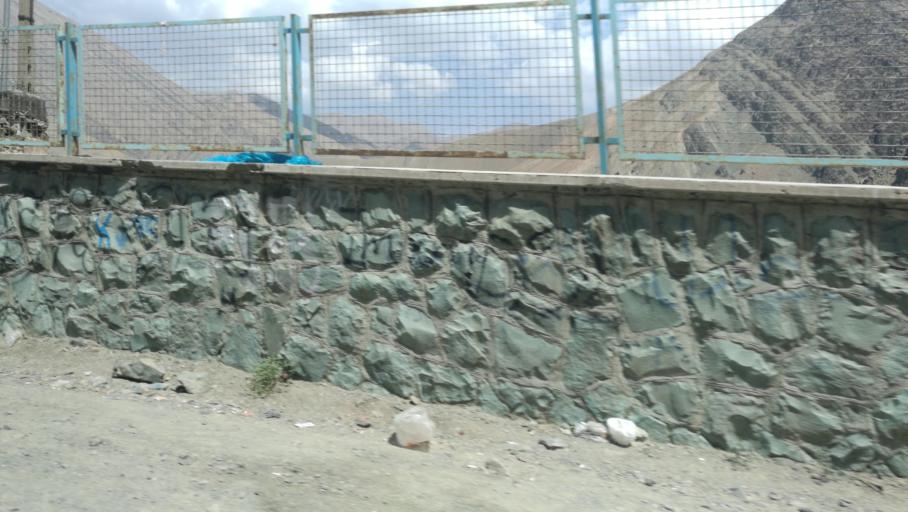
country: IR
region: Alborz
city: Karaj
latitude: 35.9631
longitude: 51.0929
